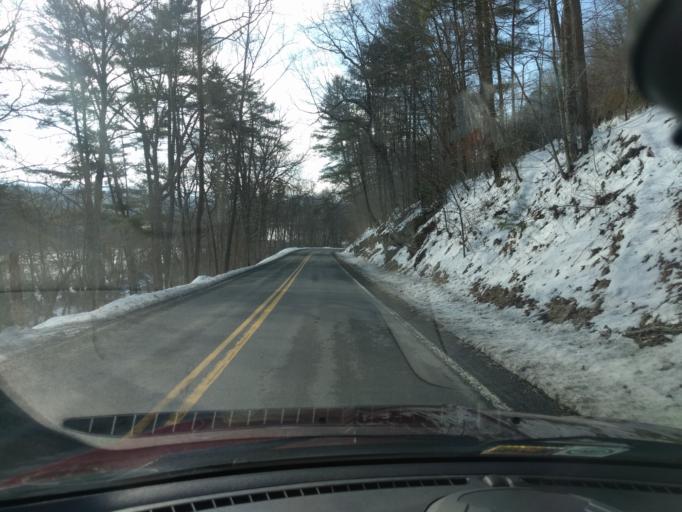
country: US
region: Virginia
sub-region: Bath County
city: Warm Springs
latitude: 38.0808
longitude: -79.8450
